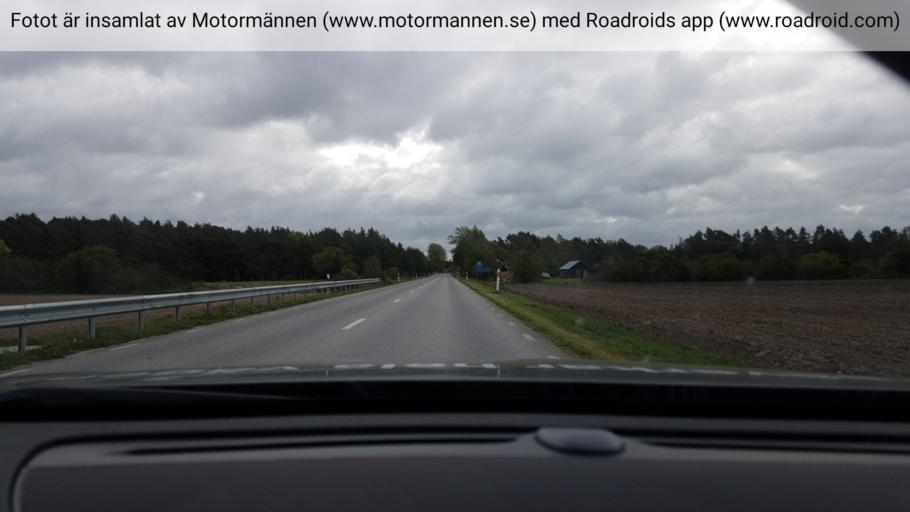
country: SE
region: Gotland
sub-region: Gotland
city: Klintehamn
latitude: 57.4021
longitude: 18.1845
